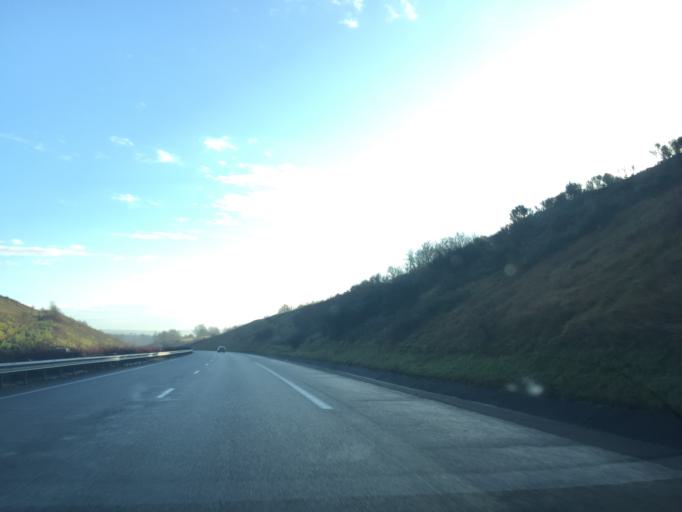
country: FR
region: Aquitaine
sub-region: Departement de la Dordogne
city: Thenon
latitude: 45.1534
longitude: 1.0993
